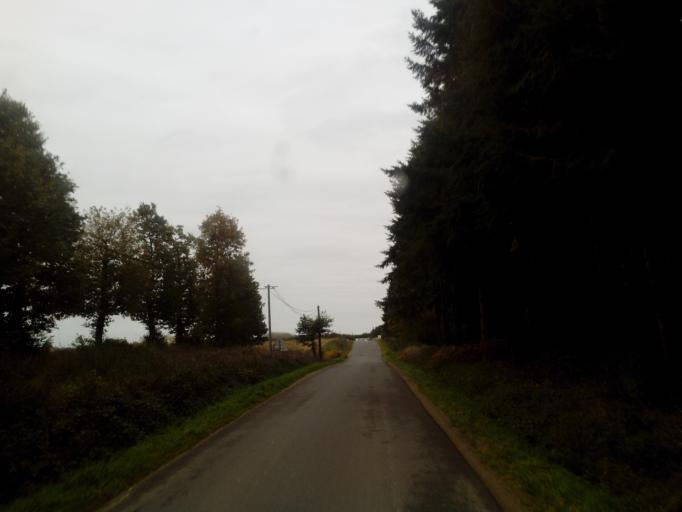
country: FR
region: Brittany
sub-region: Departement du Morbihan
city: Mauron
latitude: 48.0676
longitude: -2.3057
